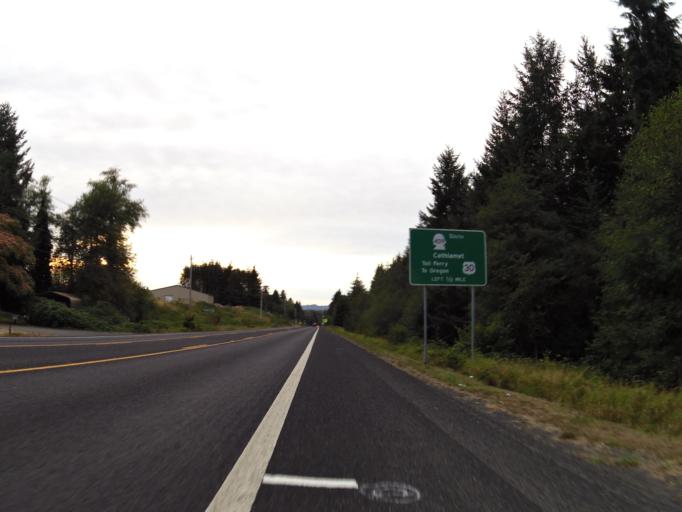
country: US
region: Washington
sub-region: Wahkiakum County
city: Cathlamet
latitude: 46.2002
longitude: -123.3725
